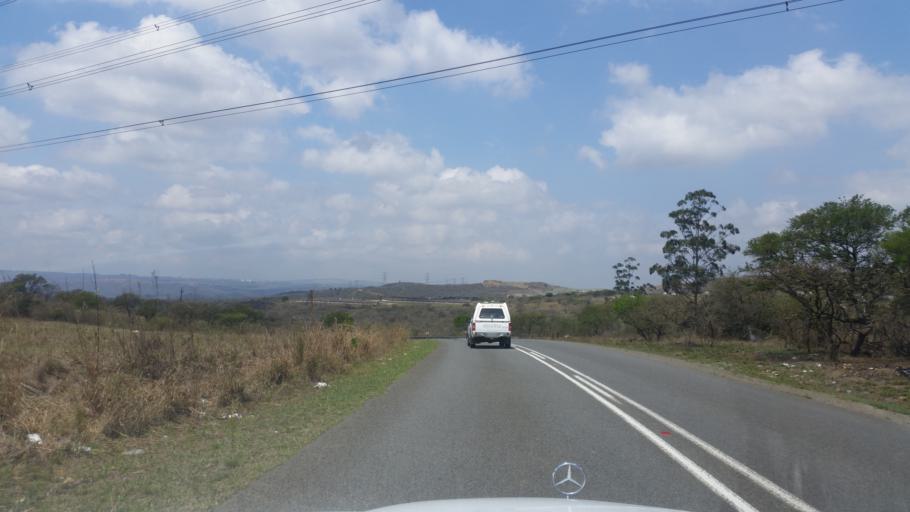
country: ZA
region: KwaZulu-Natal
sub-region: uMgungundlovu District Municipality
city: Camperdown
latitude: -29.6974
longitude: 30.4923
